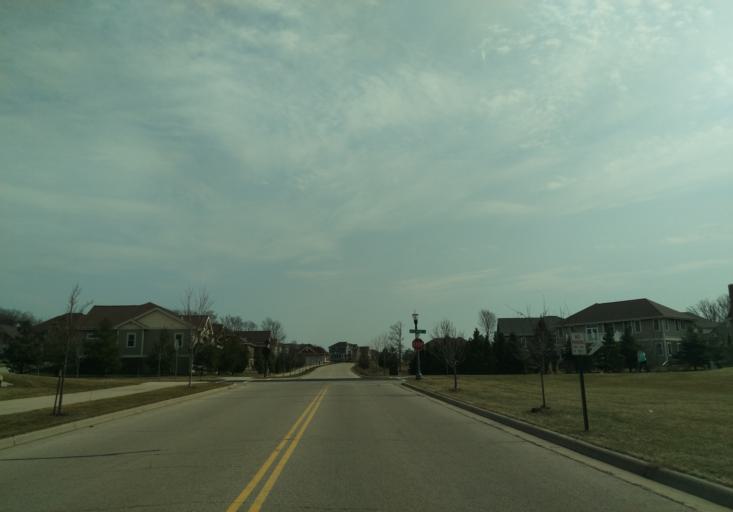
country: US
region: Wisconsin
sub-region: Dane County
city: Waunakee
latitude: 43.1688
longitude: -89.4439
